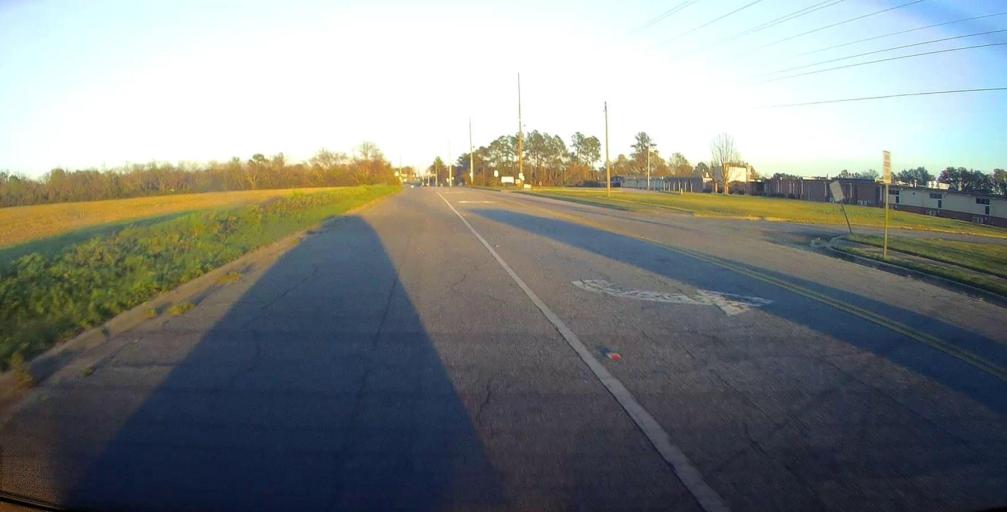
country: US
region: Georgia
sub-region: Crisp County
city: Cordele
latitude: 31.9552
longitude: -83.7979
